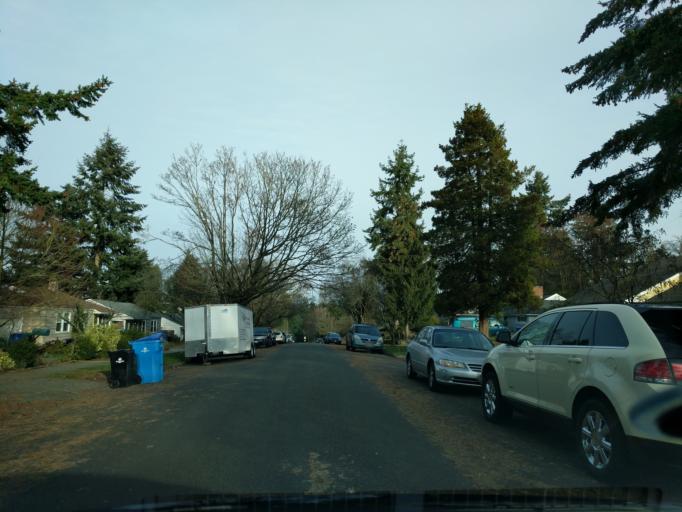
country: US
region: Washington
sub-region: King County
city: Shoreline
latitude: 47.7533
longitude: -122.3267
